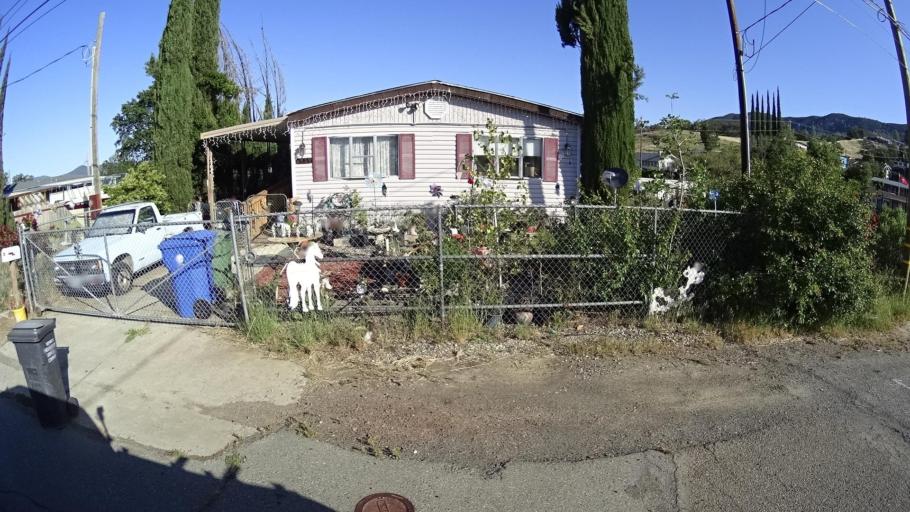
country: US
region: California
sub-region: Lake County
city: Nice
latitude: 39.1267
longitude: -122.8608
